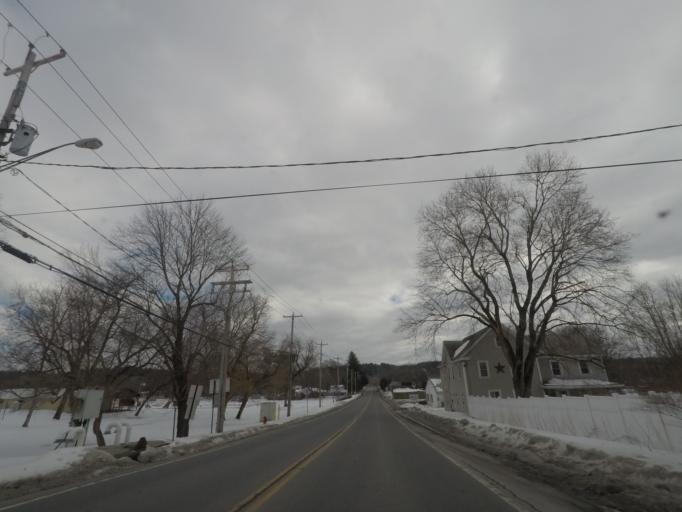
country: US
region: New York
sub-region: Saratoga County
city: Schuylerville
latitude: 43.0995
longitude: -73.5794
